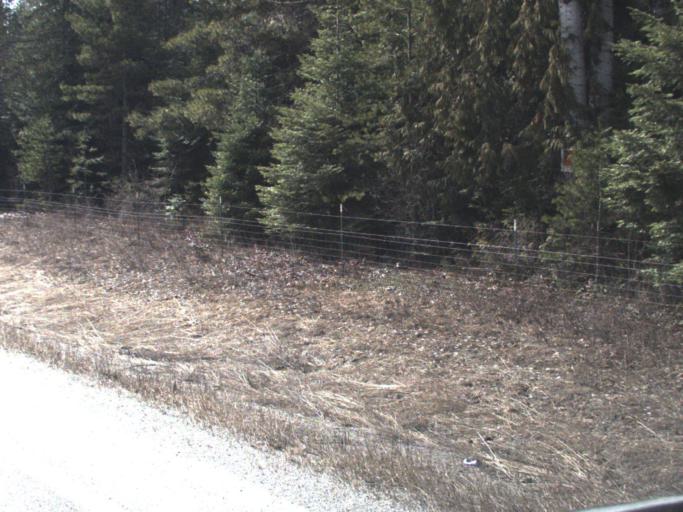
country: US
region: Washington
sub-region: Stevens County
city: Chewelah
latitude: 48.6368
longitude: -117.3707
